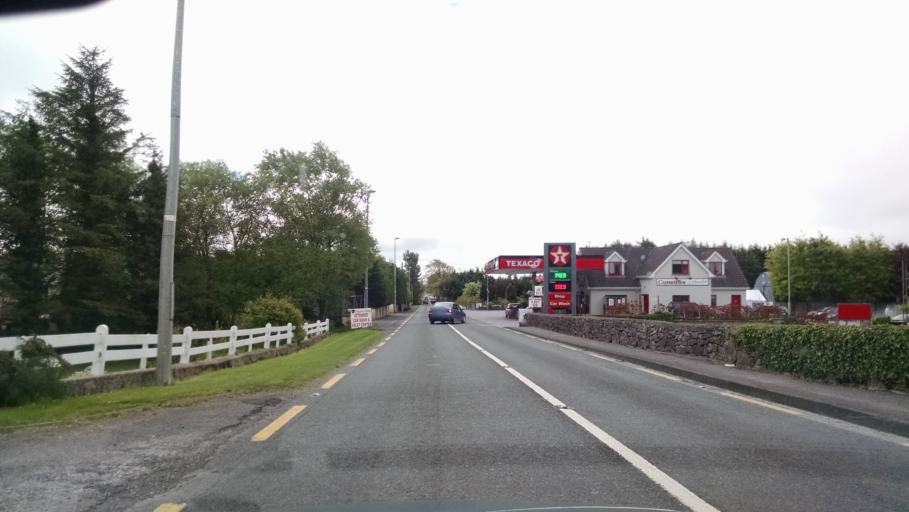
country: IE
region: Connaught
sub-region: County Galway
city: Claregalway
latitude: 53.3750
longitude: -9.0162
